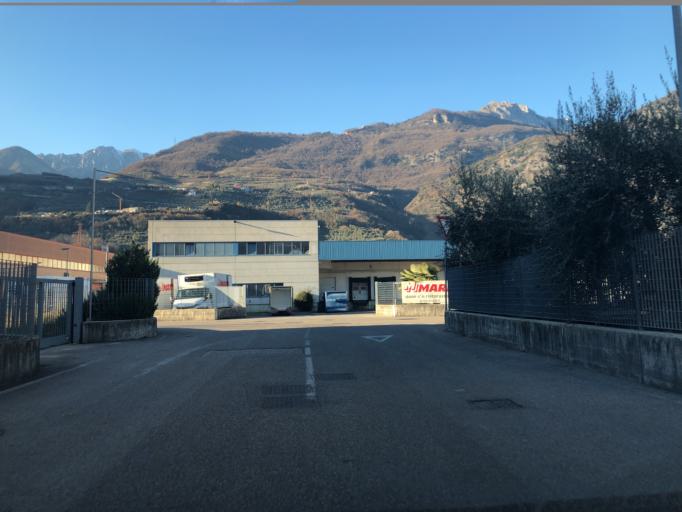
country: IT
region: Trentino-Alto Adige
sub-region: Provincia di Trento
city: Arco
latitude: 45.9126
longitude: 10.8633
